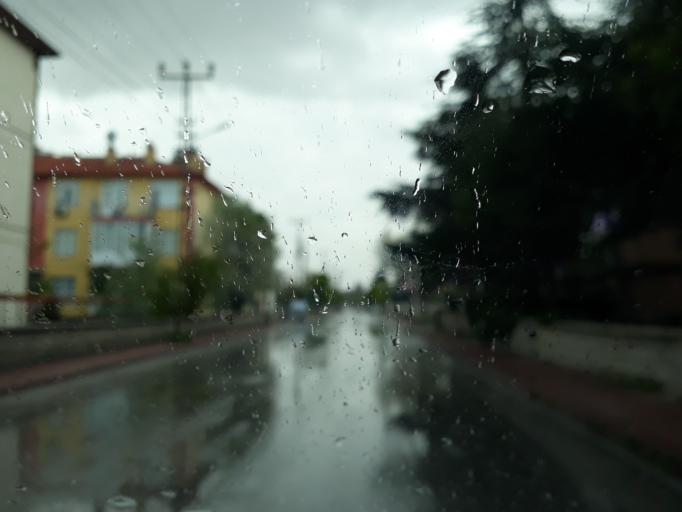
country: TR
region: Konya
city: Selcuklu
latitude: 37.9129
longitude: 32.4949
